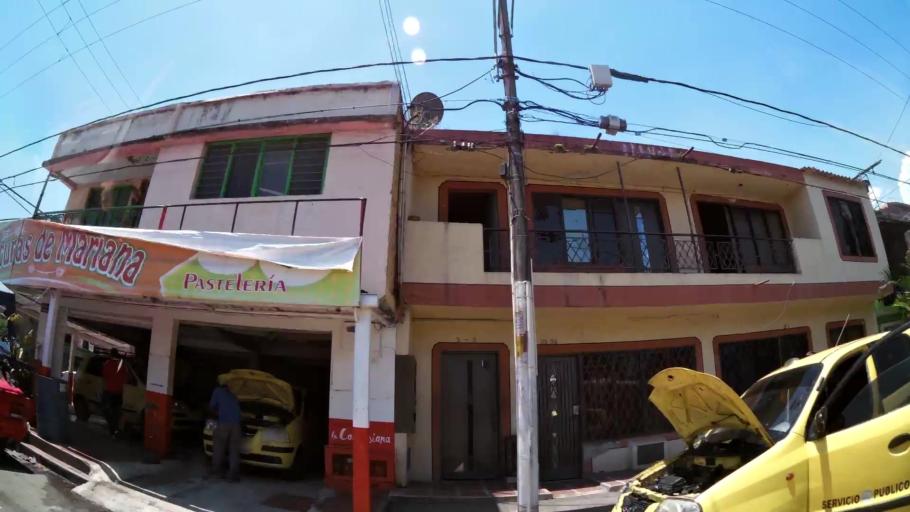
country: CO
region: Valle del Cauca
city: Cali
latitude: 3.4350
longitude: -76.5060
